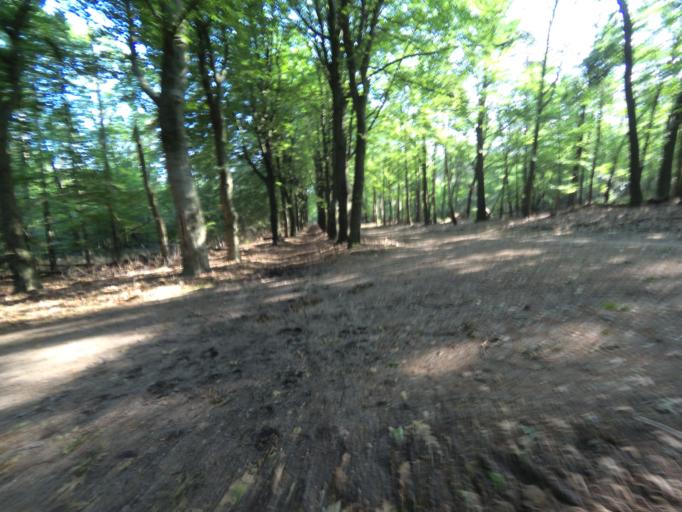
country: NL
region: Gelderland
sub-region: Gemeente Apeldoorn
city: Beekbergen
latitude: 52.1707
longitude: 5.8724
